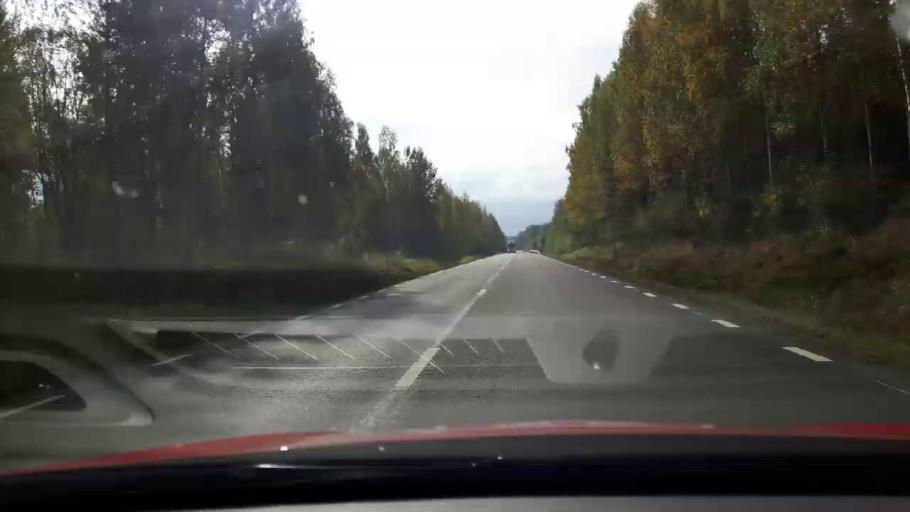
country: SE
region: Gaevleborg
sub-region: Bollnas Kommun
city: Arbra
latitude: 61.4805
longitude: 16.3654
